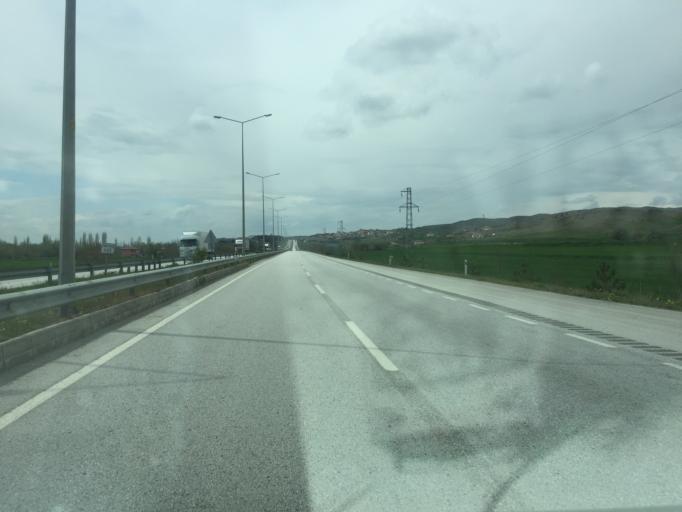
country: TR
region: Corum
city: Sungurlu
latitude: 40.1774
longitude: 34.4413
